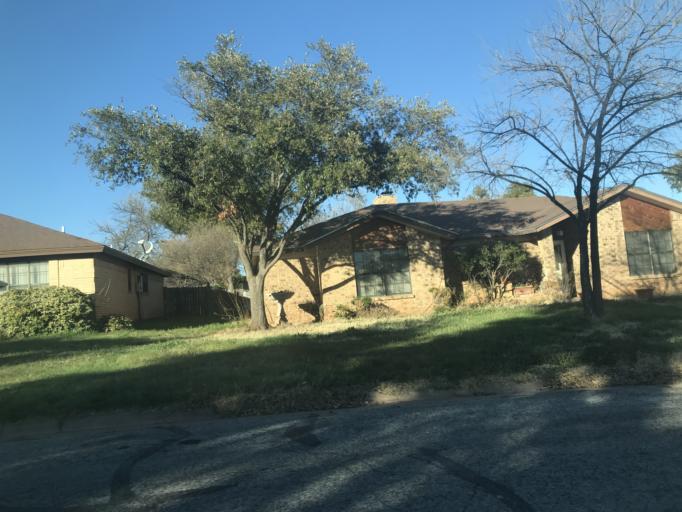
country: US
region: Texas
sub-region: Tom Green County
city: San Angelo
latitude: 31.4255
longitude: -100.4923
